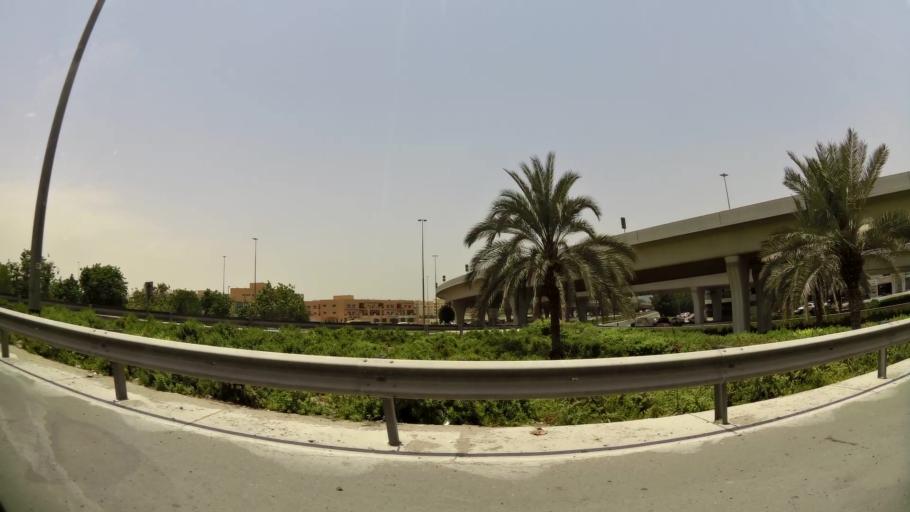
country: AE
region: Ash Shariqah
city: Sharjah
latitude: 25.2188
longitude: 55.3762
